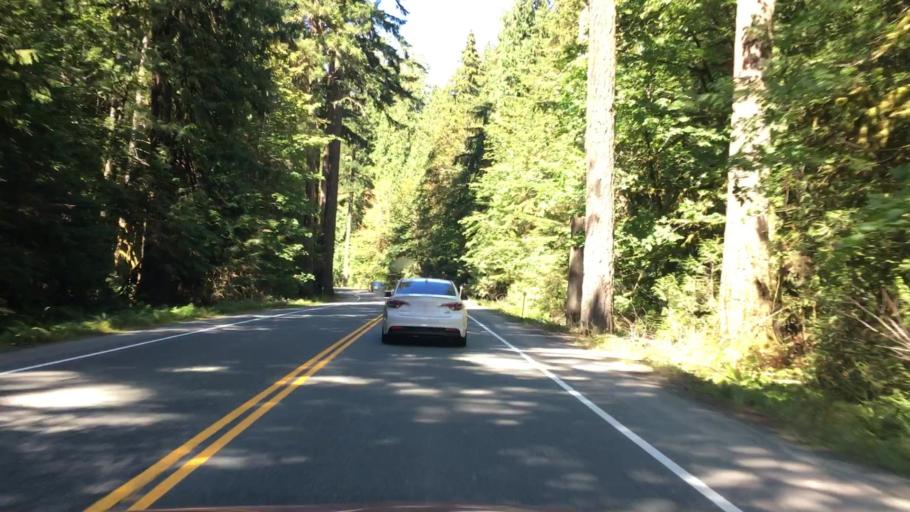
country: CA
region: British Columbia
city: Port Alberni
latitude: 49.2730
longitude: -124.6751
